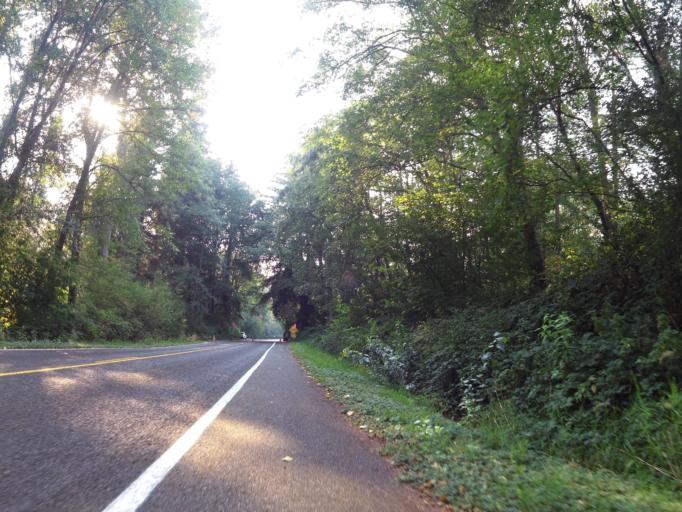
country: US
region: Washington
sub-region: Whatcom County
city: Birch Bay
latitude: 48.9033
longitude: -122.7587
